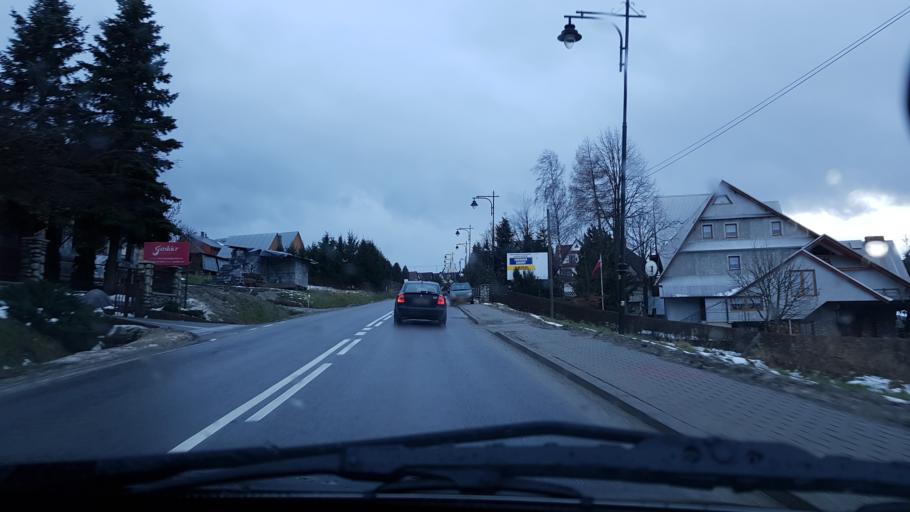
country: PL
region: Lesser Poland Voivodeship
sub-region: Powiat tatrzanski
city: Bukowina Tatrzanska
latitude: 49.3468
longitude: 20.1158
